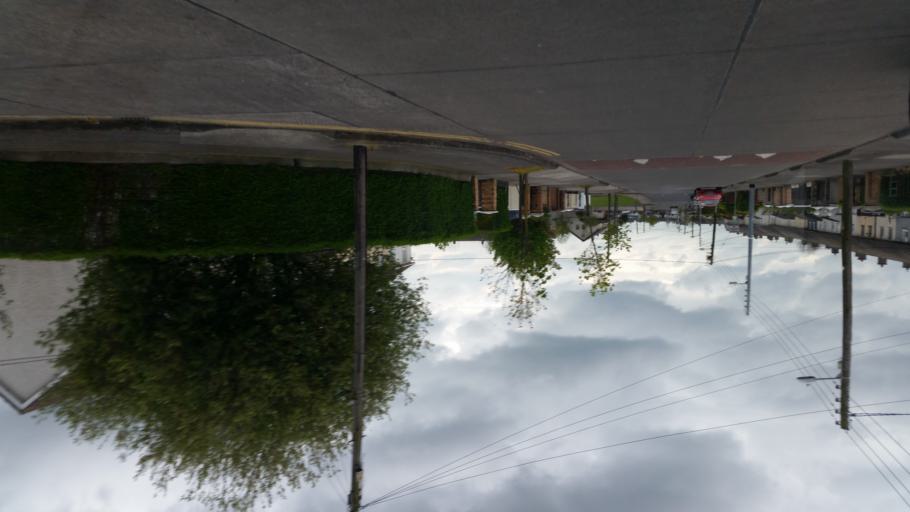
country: IE
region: Leinster
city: Artane
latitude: 53.3931
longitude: -6.2254
